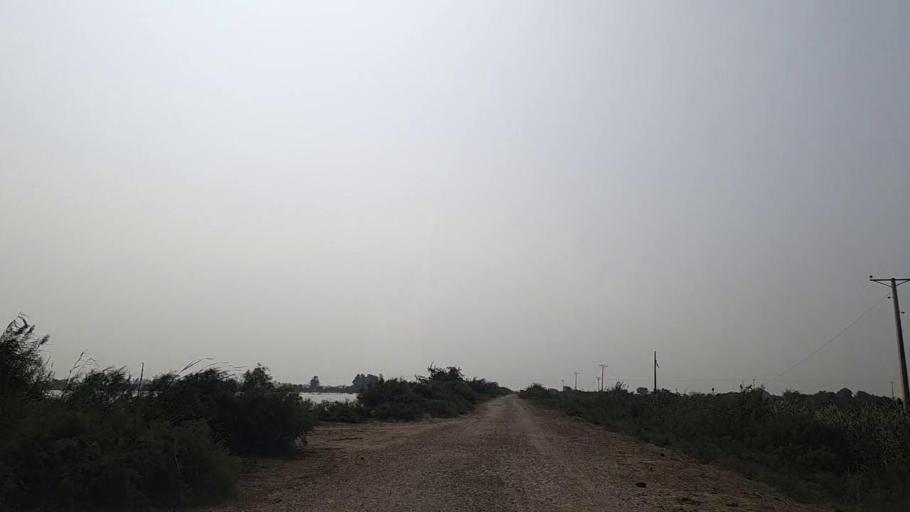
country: PK
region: Sindh
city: Thatta
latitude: 24.6958
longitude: 67.8009
